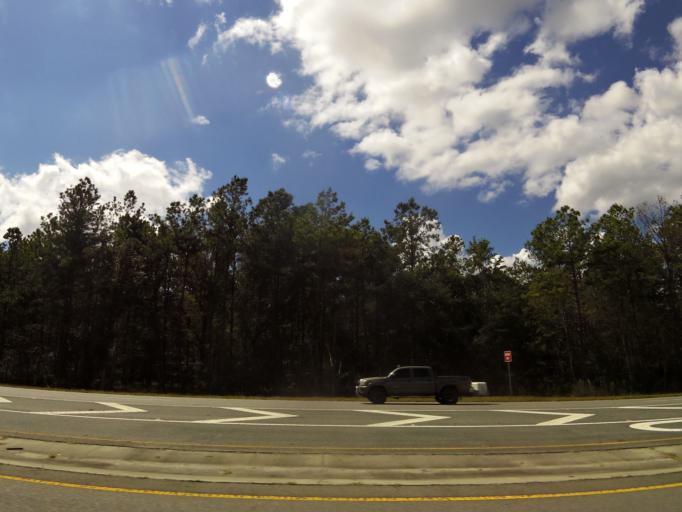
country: US
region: Georgia
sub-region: Charlton County
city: Folkston
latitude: 30.7997
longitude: -81.9880
